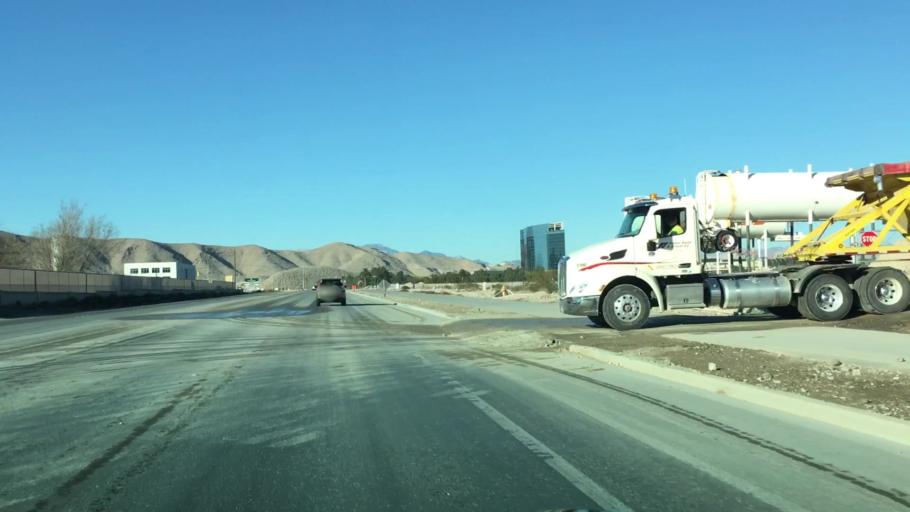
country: US
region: Nevada
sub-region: Clark County
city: Enterprise
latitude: 35.9629
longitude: -115.1609
